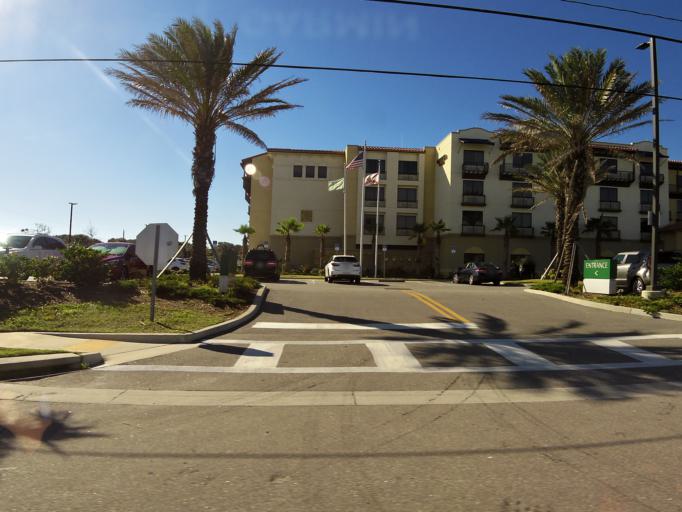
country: US
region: Florida
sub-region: Saint Johns County
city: Saint Augustine Beach
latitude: 29.8485
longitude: -81.2674
